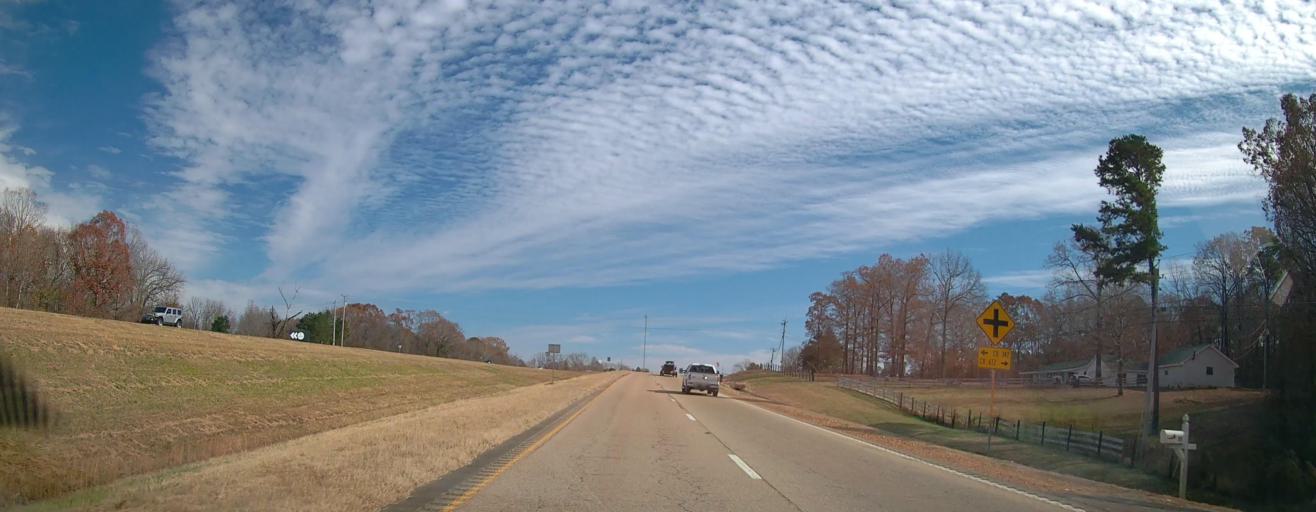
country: US
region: Mississippi
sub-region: Tippah County
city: Ripley
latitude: 34.9492
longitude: -88.8143
